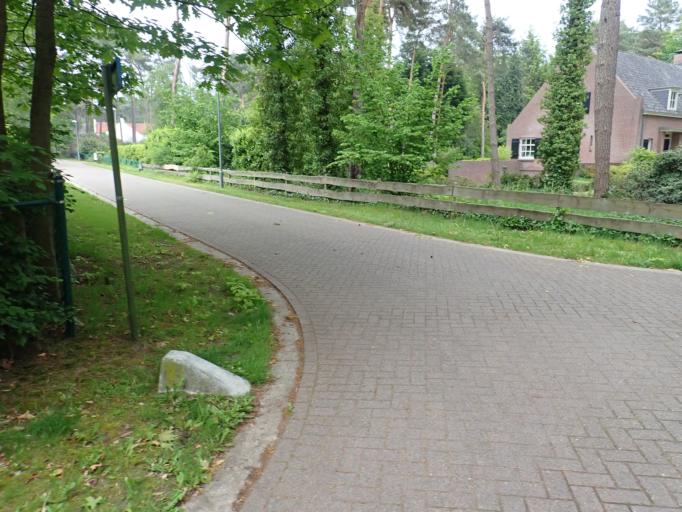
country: BE
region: Flanders
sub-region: Provincie Antwerpen
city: Oud-Turnhout
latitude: 51.3157
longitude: 5.0031
